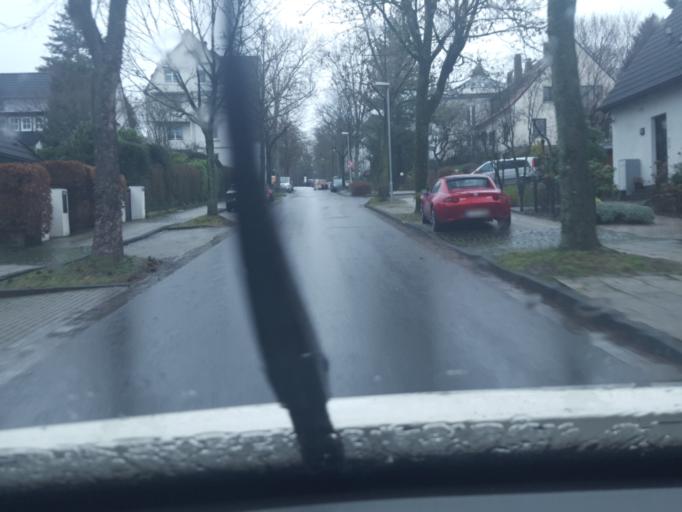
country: DE
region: North Rhine-Westphalia
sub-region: Regierungsbezirk Dusseldorf
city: Essen
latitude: 51.3945
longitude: 7.0043
